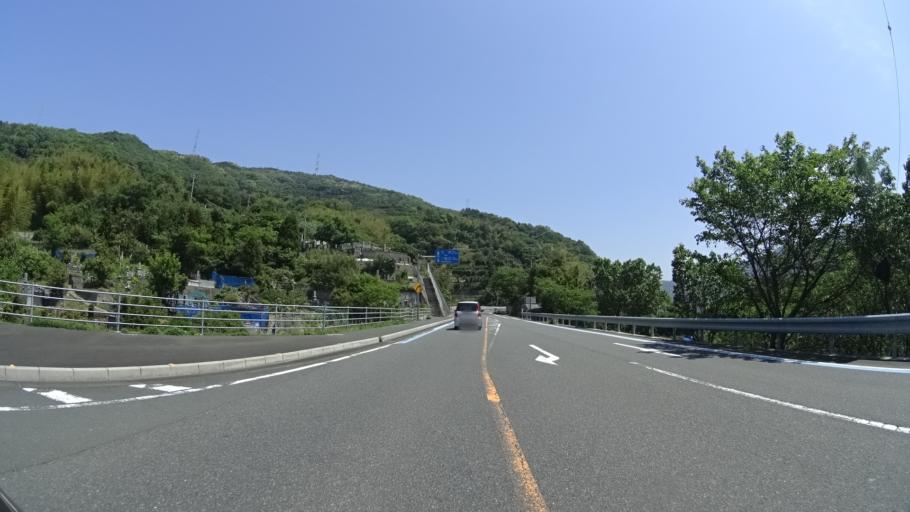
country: JP
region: Ehime
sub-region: Nishiuwa-gun
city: Ikata-cho
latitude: 33.4903
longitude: 132.3516
